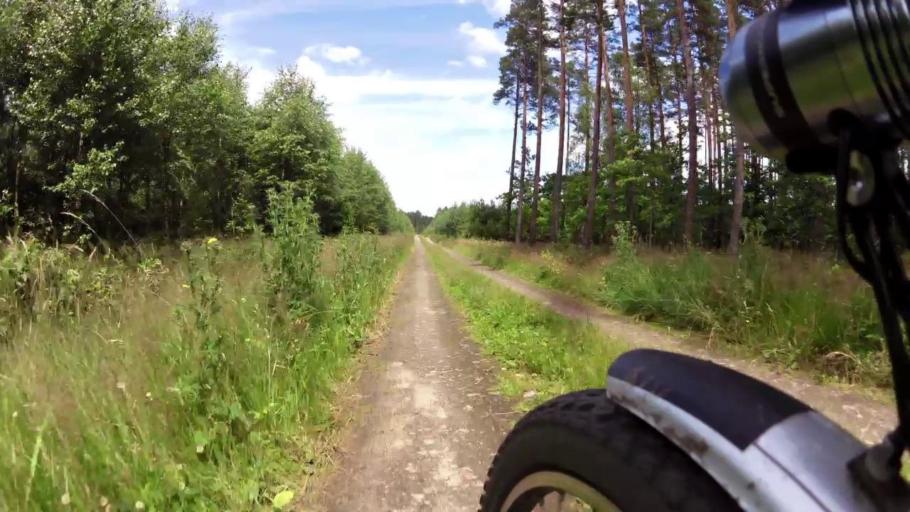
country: PL
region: West Pomeranian Voivodeship
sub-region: Powiat swidwinski
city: Rabino
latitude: 53.8901
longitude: 15.9928
